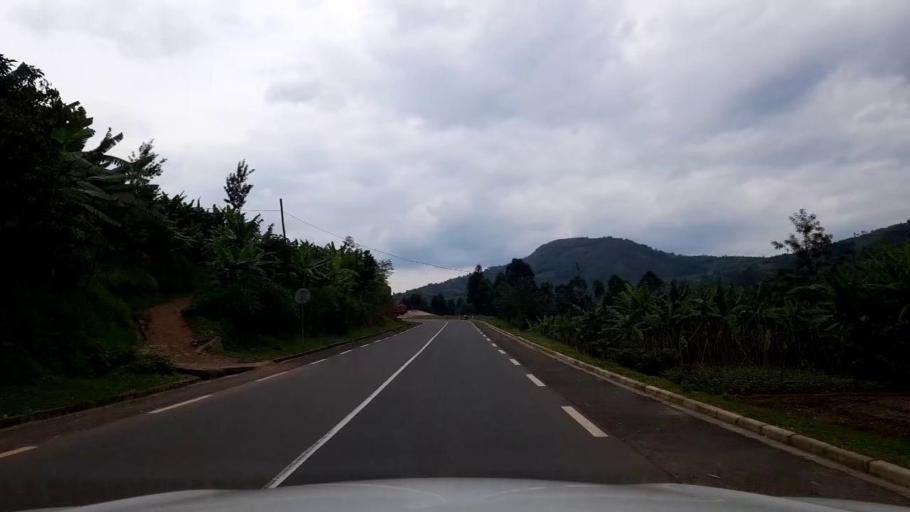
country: RW
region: Western Province
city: Kibuye
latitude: -1.9171
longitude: 29.3692
